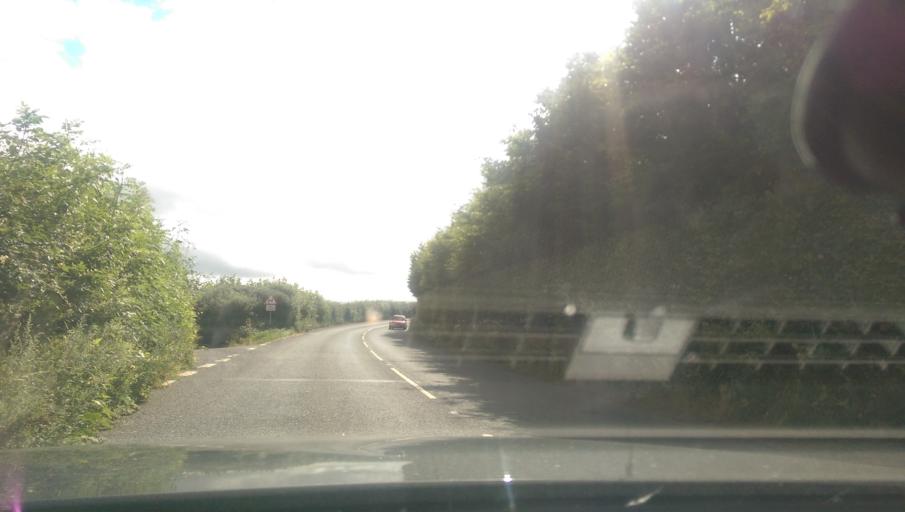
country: GB
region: England
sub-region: Devon
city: Okehampton
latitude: 50.7363
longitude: -3.9413
